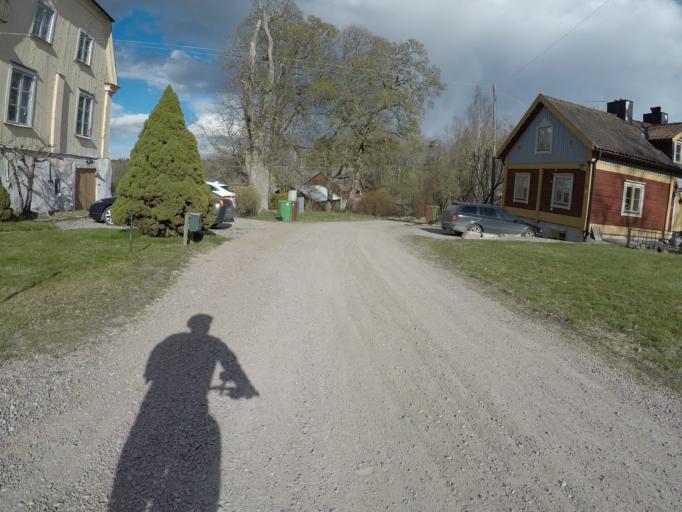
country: SE
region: Soedermanland
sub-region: Eskilstuna Kommun
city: Kvicksund
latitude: 59.4730
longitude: 16.2944
